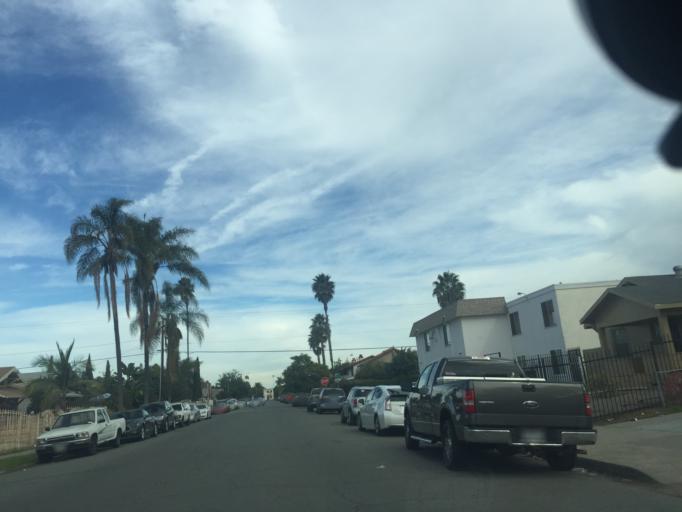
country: US
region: California
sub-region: San Diego County
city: Lemon Grove
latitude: 32.7508
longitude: -117.0987
